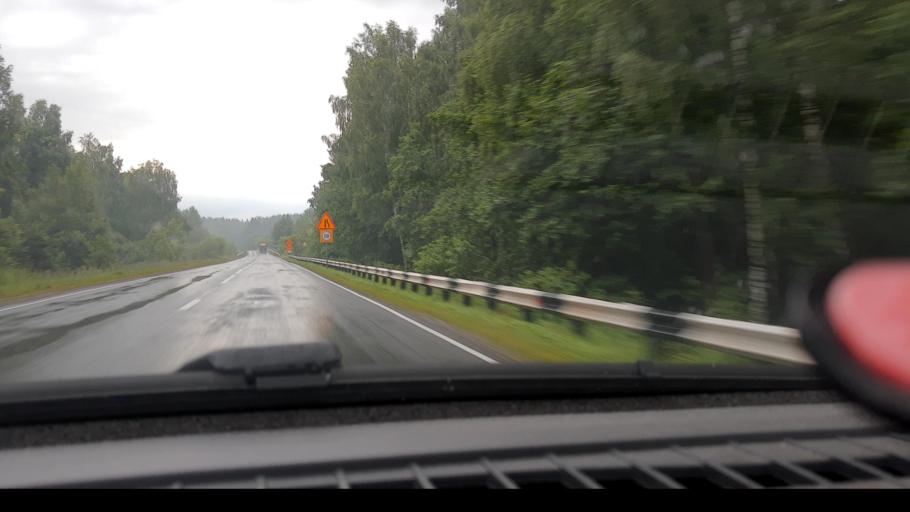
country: RU
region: Nizjnij Novgorod
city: Gorodets
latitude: 56.6142
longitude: 43.5724
